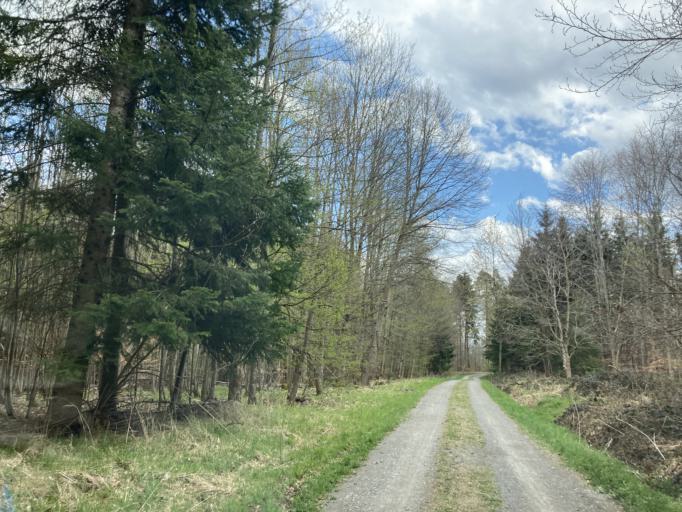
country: DE
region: Baden-Wuerttemberg
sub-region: Tuebingen Region
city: Dettenhausen
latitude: 48.5820
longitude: 9.1183
